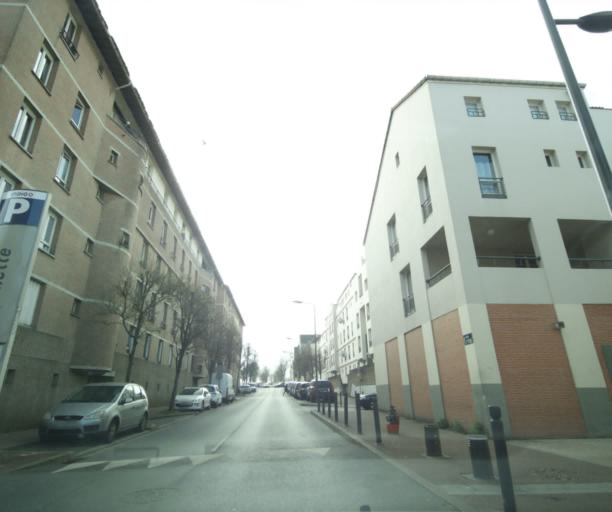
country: FR
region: Ile-de-France
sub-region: Departement du Val-d'Oise
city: Vaureal
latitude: 49.0480
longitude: 2.0325
